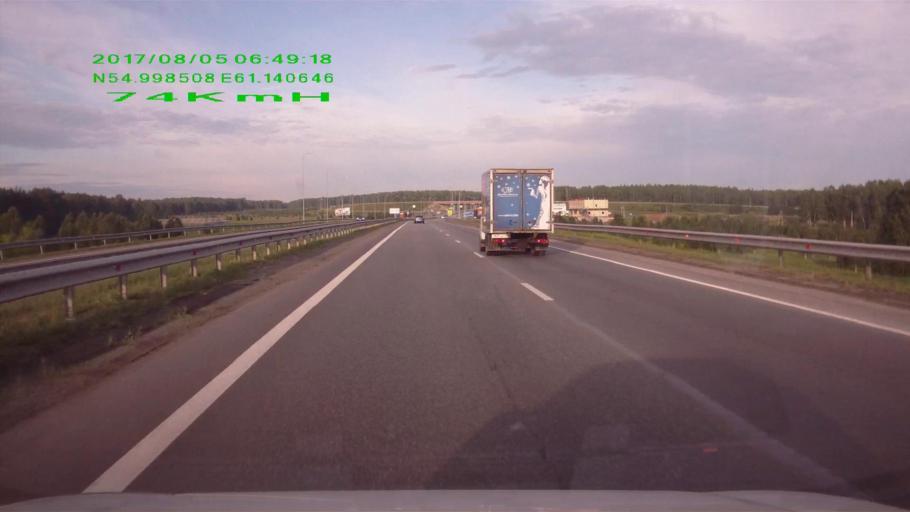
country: RU
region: Chelyabinsk
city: Poletayevo
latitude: 54.9984
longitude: 61.1404
